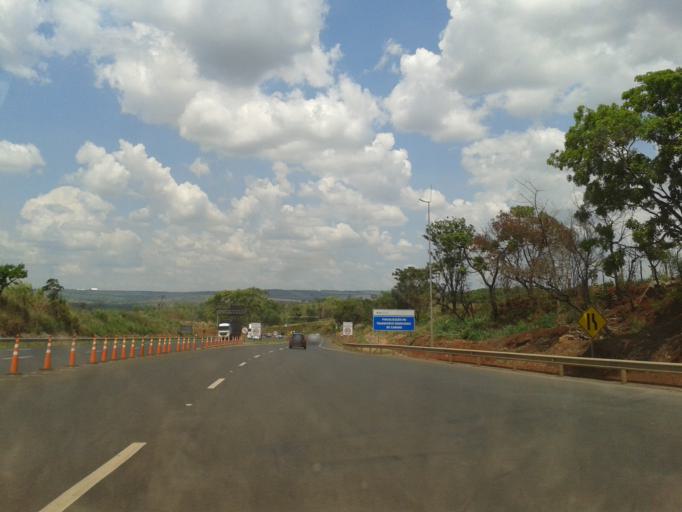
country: BR
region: Minas Gerais
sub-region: Araguari
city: Araguari
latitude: -18.7515
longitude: -48.2374
